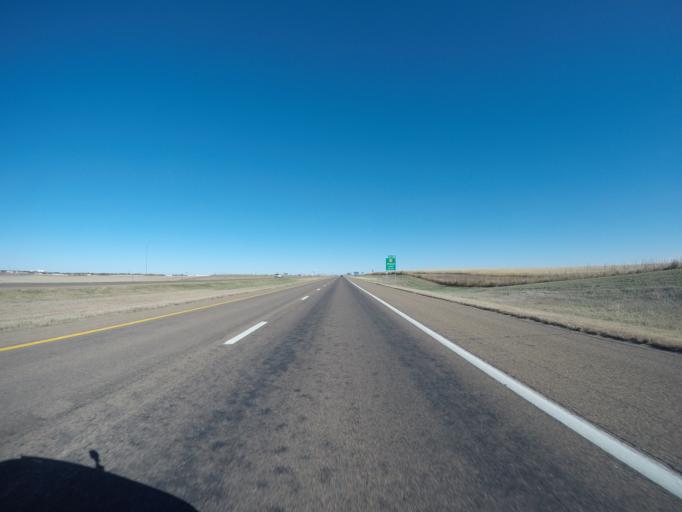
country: US
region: Kansas
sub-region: Thomas County
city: Colby
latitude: 39.3647
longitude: -101.0727
